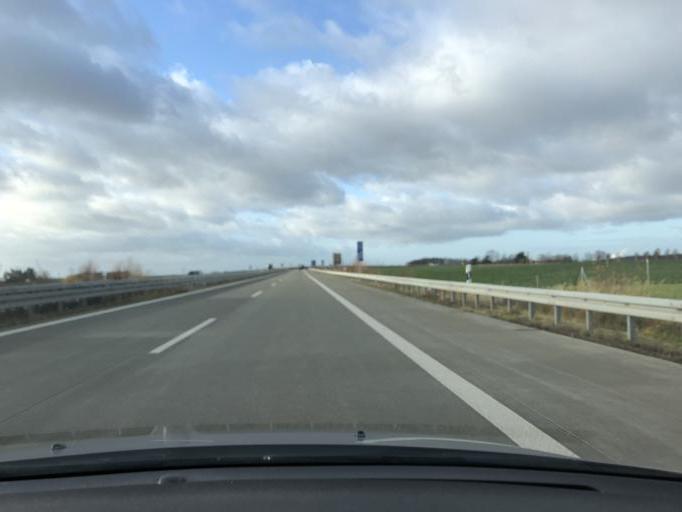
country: DE
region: Saxony
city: Geithain
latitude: 51.0471
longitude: 12.6501
